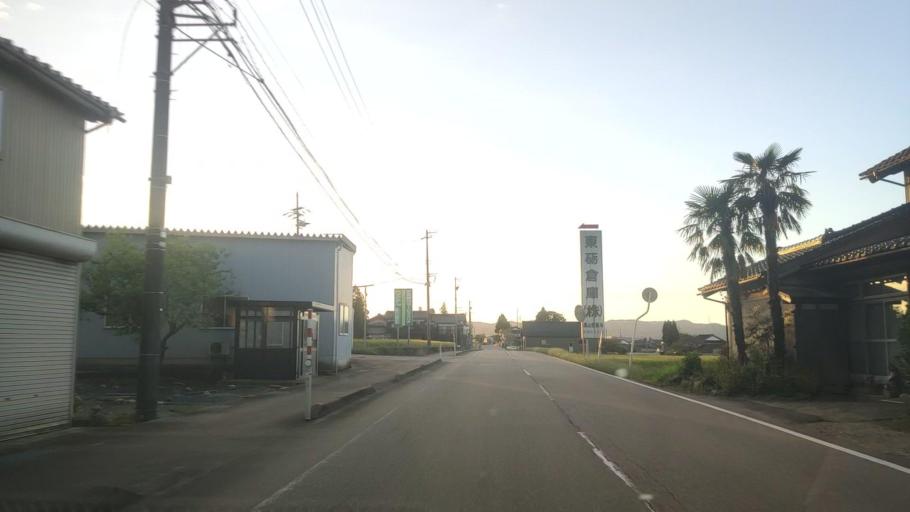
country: JP
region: Toyama
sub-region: Oyabe Shi
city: Oyabe
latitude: 36.6290
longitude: 136.8776
